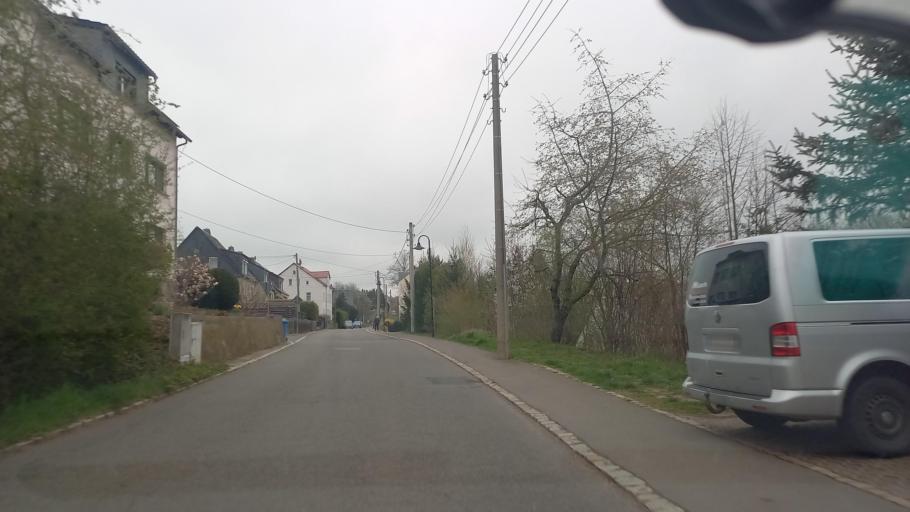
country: DE
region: Saxony
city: Reinsdorf
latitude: 50.6972
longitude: 12.5657
